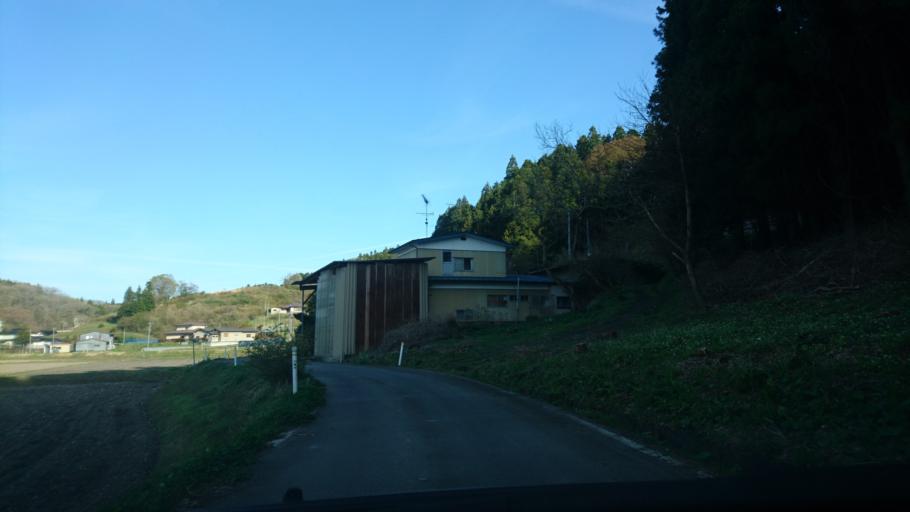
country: JP
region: Iwate
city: Ichinoseki
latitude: 38.8961
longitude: 141.2967
